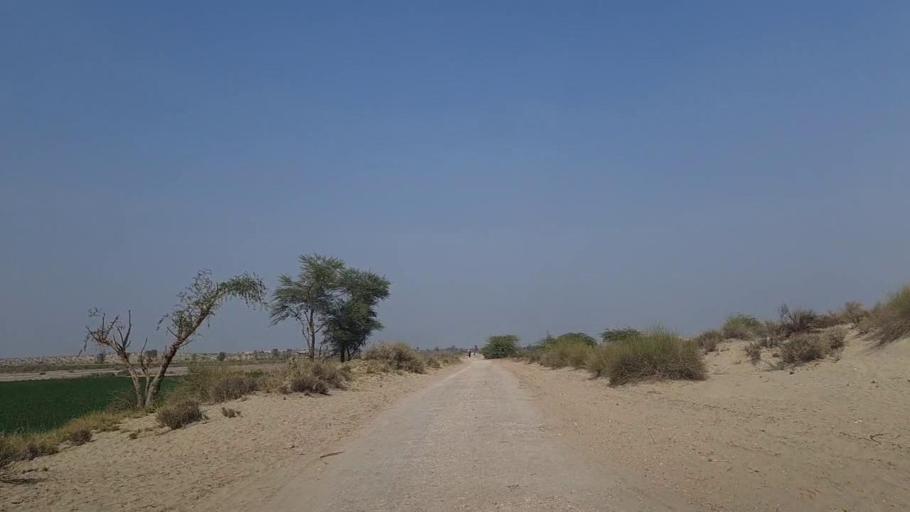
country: PK
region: Sindh
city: Daur
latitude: 26.4752
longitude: 68.4509
